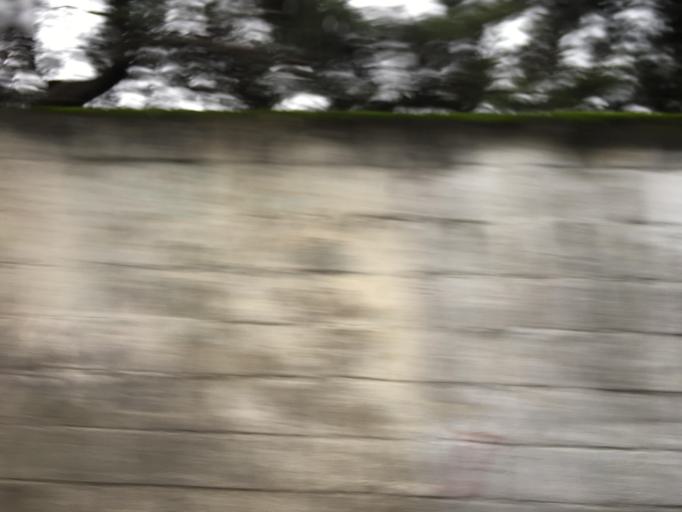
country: GT
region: Sacatepequez
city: Pastores
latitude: 14.6007
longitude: -90.7602
